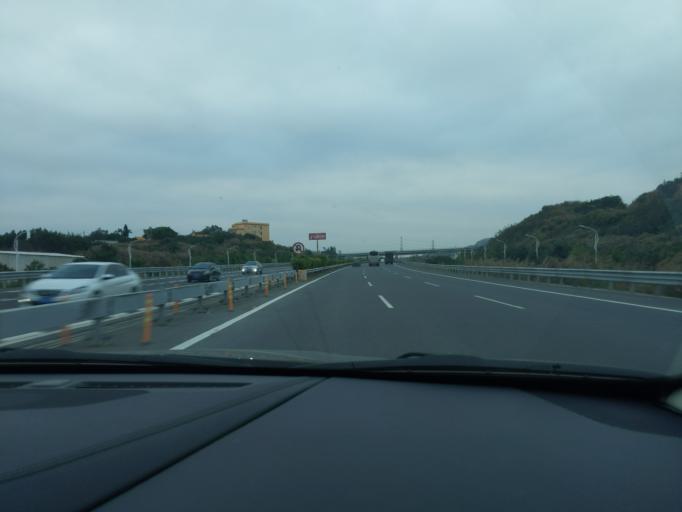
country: CN
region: Fujian
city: Neikeng
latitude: 24.7837
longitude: 118.4944
